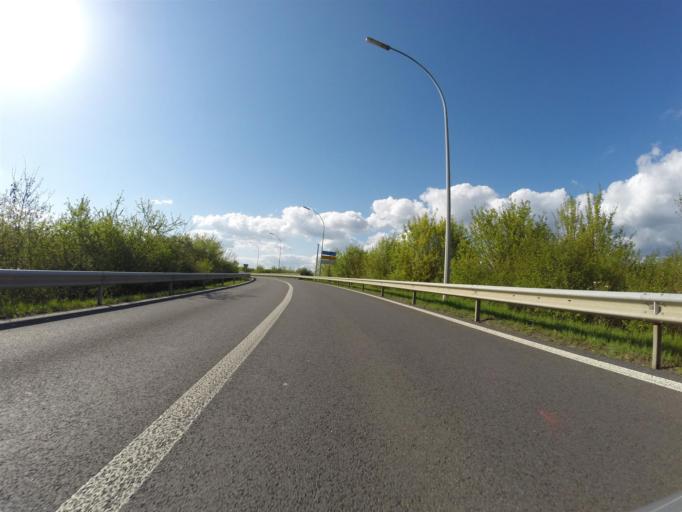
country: LU
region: Luxembourg
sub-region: Canton de Luxembourg
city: Hesperange
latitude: 49.5816
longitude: 6.1307
